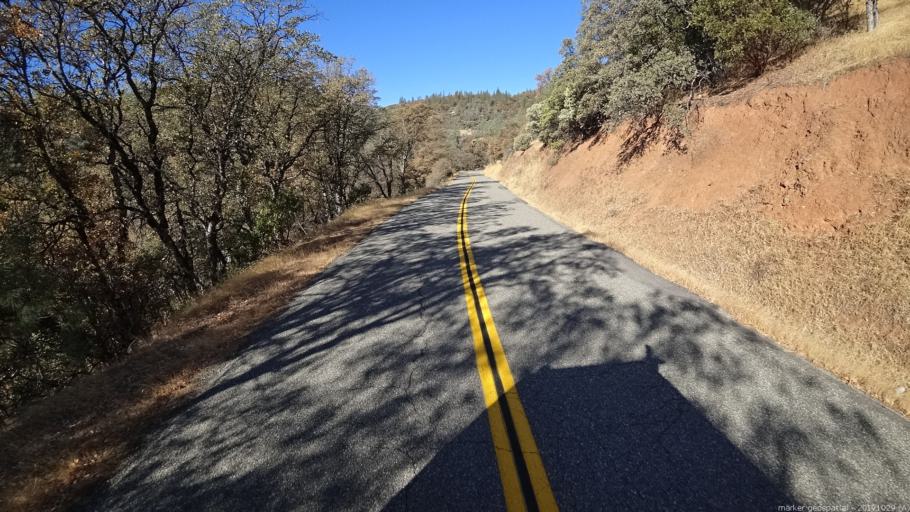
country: US
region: California
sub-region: Trinity County
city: Lewiston
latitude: 40.3690
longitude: -122.8485
